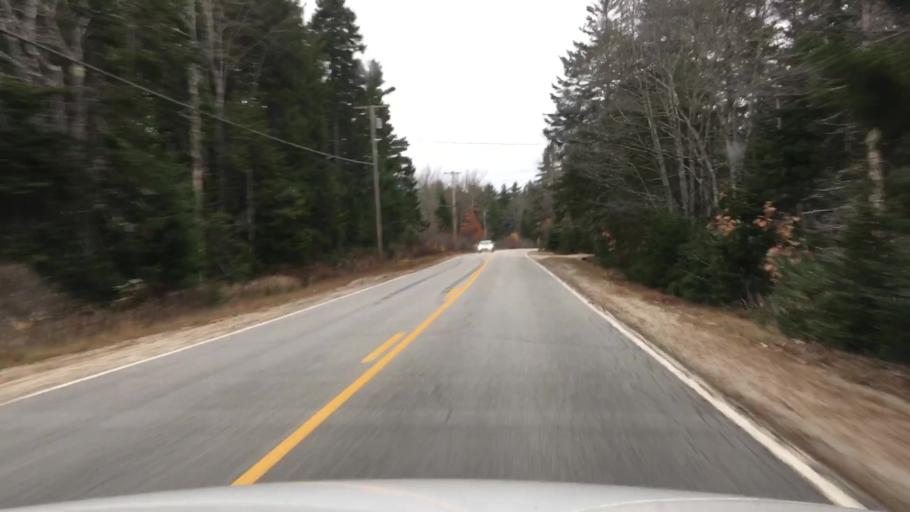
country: US
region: Maine
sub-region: Hancock County
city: Sedgwick
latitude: 44.2867
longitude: -68.5551
